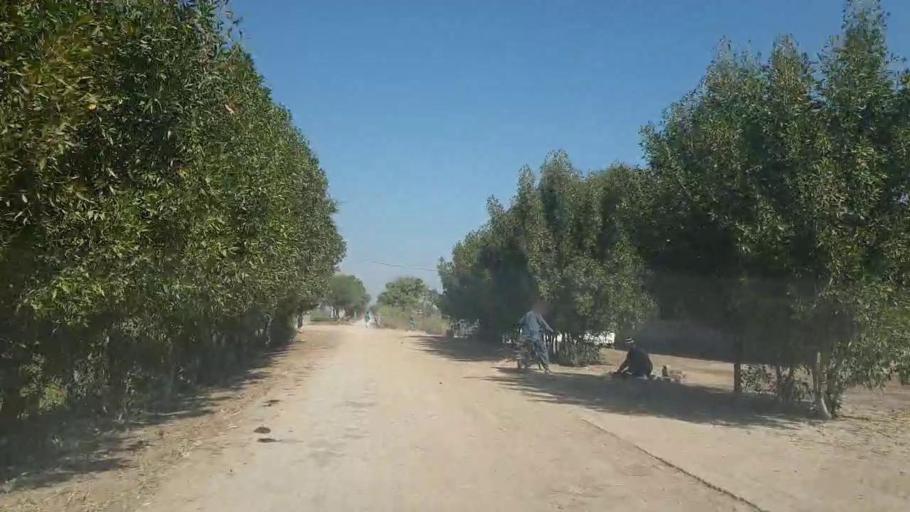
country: PK
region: Sindh
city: Mirpur Khas
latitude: 25.5450
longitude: 69.1965
